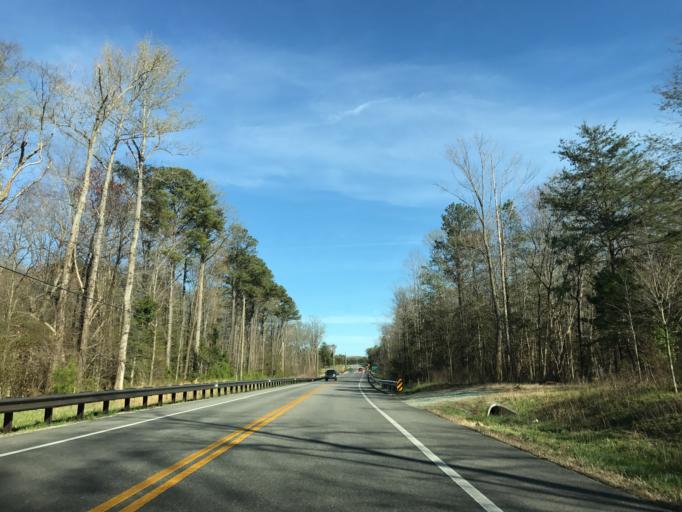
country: US
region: Maryland
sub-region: Caroline County
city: Greensboro
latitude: 39.0312
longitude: -75.7607
